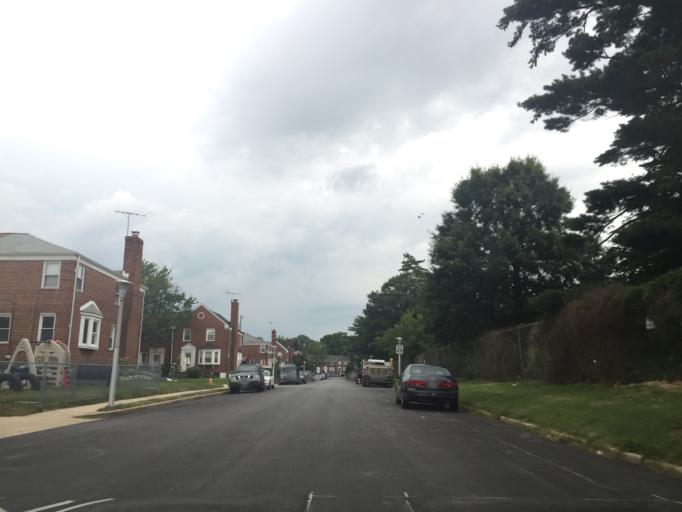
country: US
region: Maryland
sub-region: City of Baltimore
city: Baltimore
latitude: 39.3355
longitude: -76.5921
